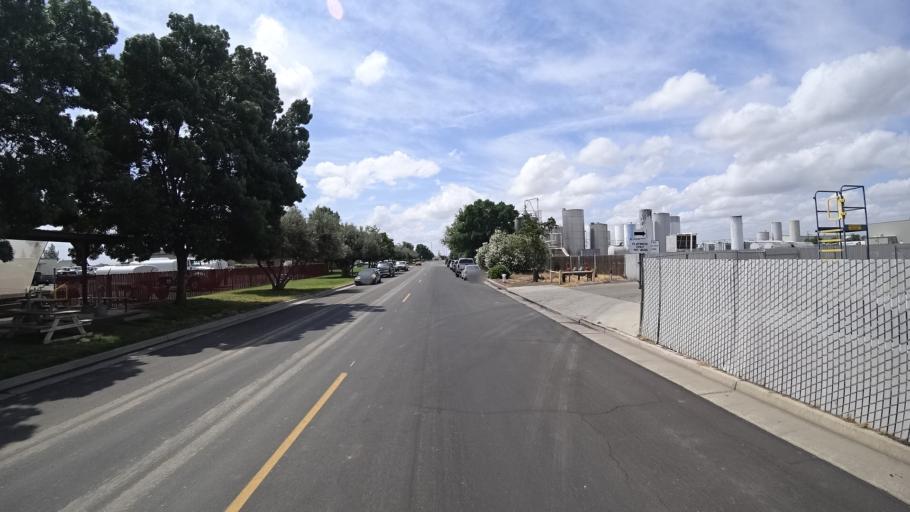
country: US
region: California
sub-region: Kings County
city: Home Garden
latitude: 36.2821
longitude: -119.6505
